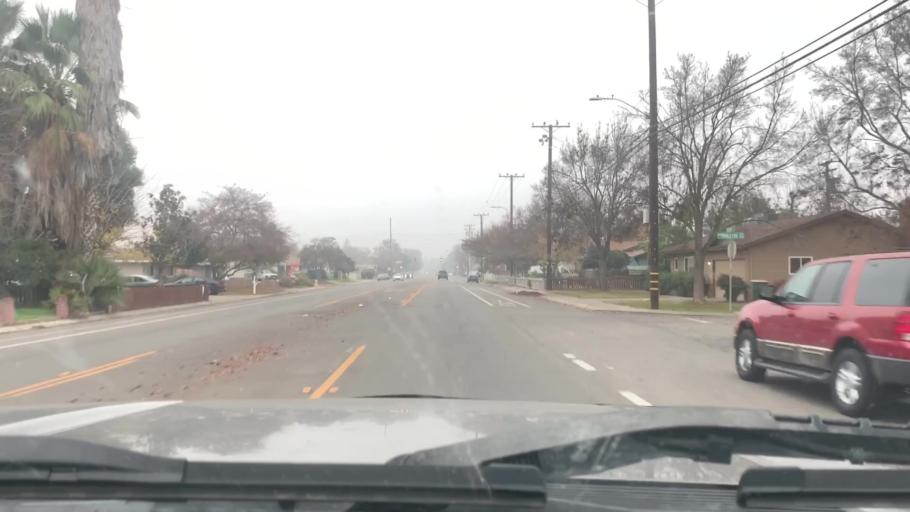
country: US
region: California
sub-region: Tulare County
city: Visalia
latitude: 36.3156
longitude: -119.3054
